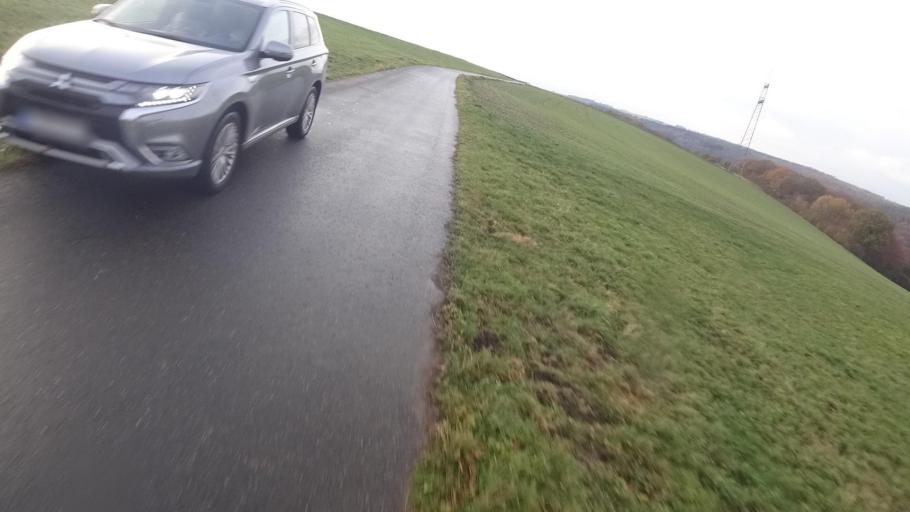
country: DE
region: Rheinland-Pfalz
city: Bickenbach
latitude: 50.1285
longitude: 7.5165
